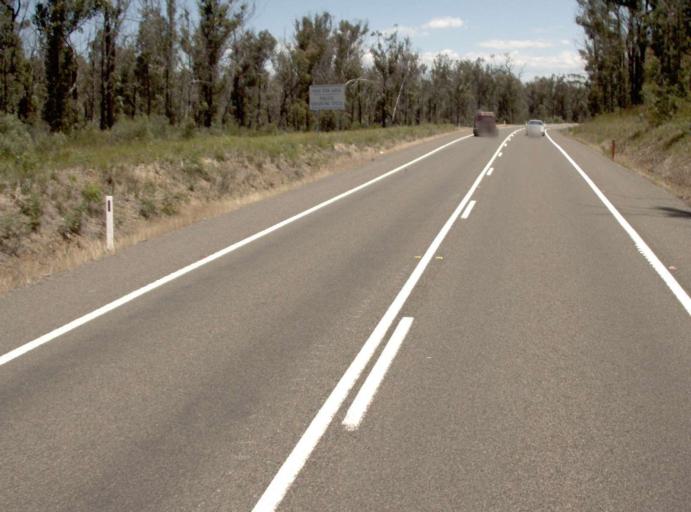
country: AU
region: Victoria
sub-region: East Gippsland
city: Lakes Entrance
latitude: -37.7518
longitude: 148.2163
